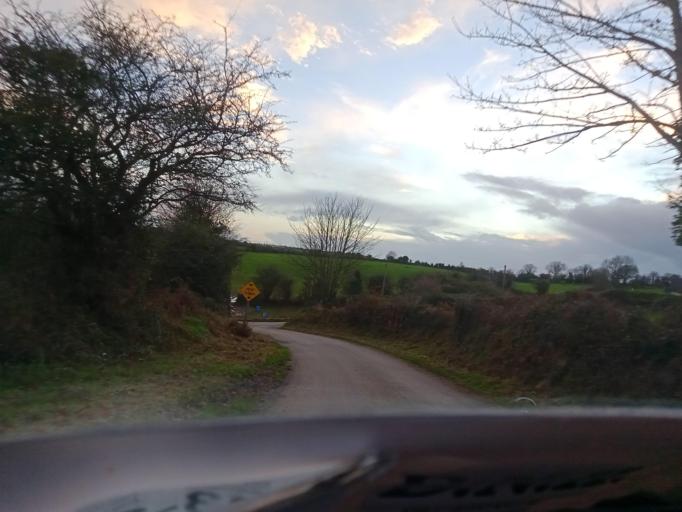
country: IE
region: Leinster
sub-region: Loch Garman
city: New Ross
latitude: 52.3343
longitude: -7.0144
